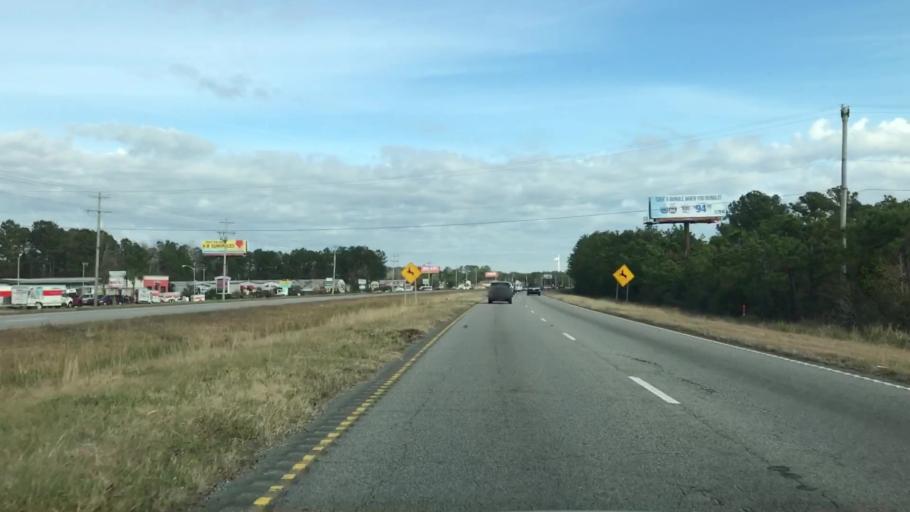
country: US
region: South Carolina
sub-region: Horry County
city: Garden City
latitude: 33.5899
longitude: -79.0261
